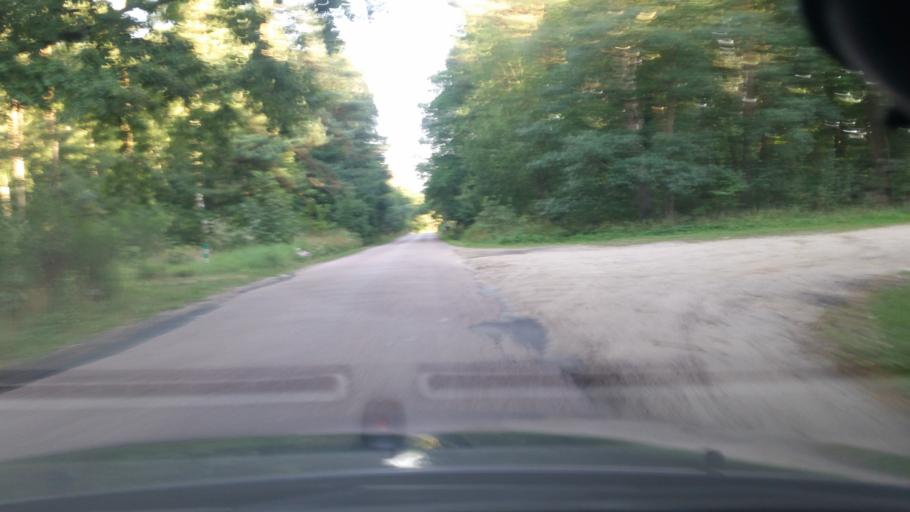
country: PL
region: Pomeranian Voivodeship
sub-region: Powiat wejherowski
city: Choczewo
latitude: 54.7597
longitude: 17.7736
